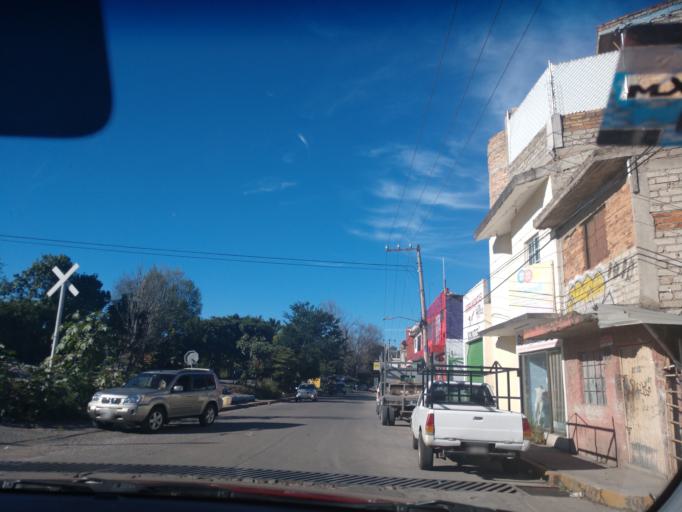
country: MX
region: Nayarit
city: Xalisco
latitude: 21.4700
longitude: -104.8701
